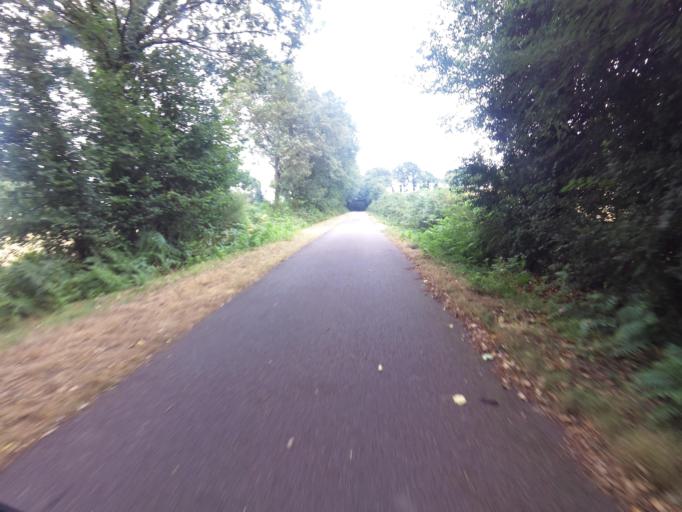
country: FR
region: Brittany
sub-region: Departement du Morbihan
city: Malestroit
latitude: 47.8161
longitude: -2.4123
